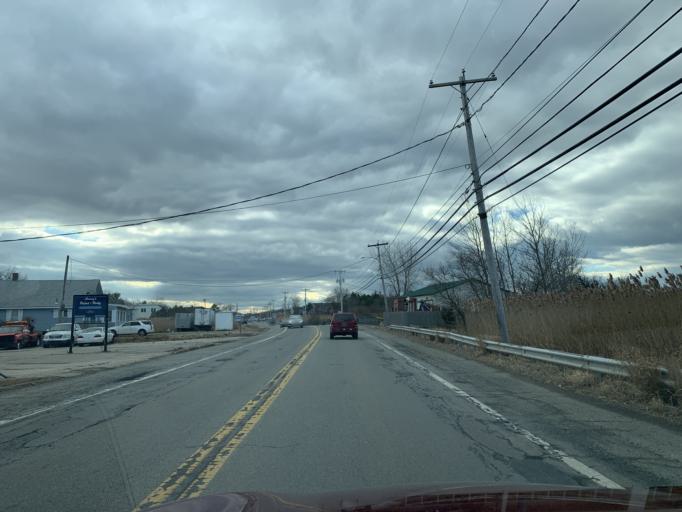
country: US
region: Massachusetts
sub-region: Essex County
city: Salisbury
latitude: 42.8306
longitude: -70.8641
